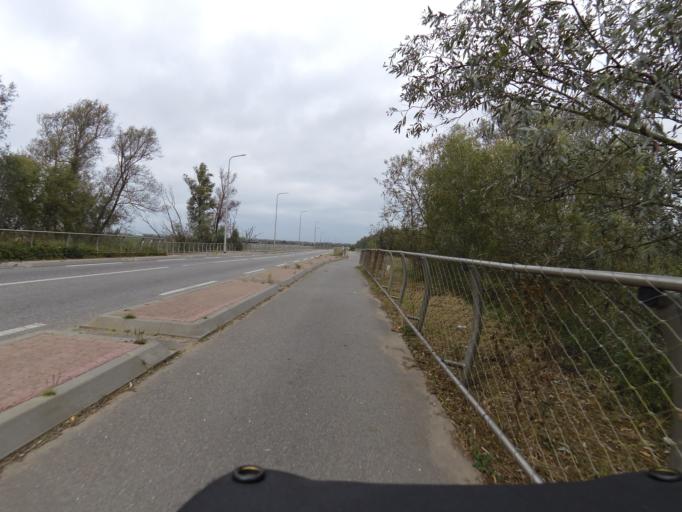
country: NL
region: Gelderland
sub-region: Gemeente Zevenaar
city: Zevenaar
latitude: 51.8919
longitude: 6.1026
